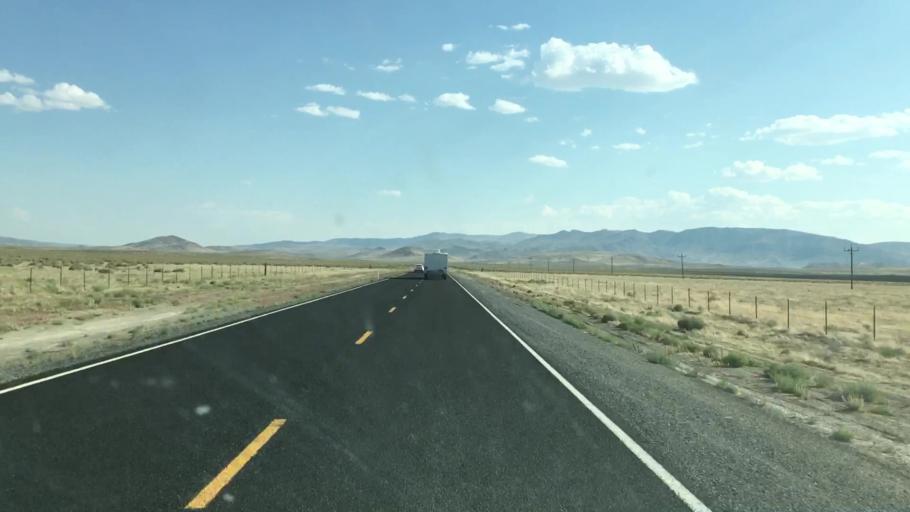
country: US
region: Nevada
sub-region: Lyon County
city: Fernley
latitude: 39.6784
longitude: -119.3337
